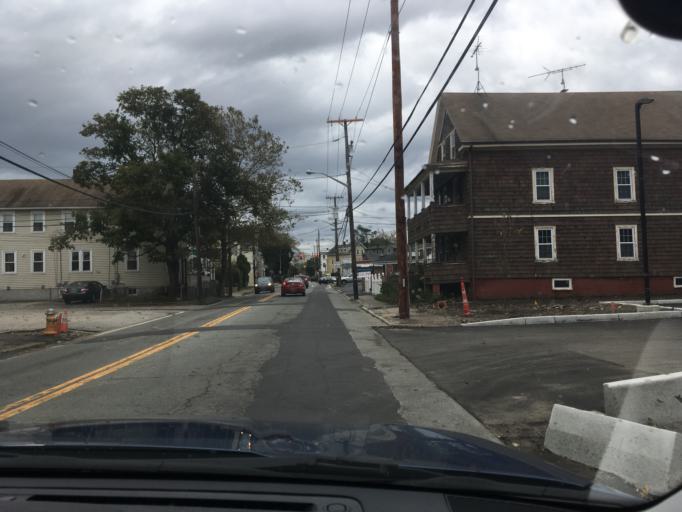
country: US
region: Rhode Island
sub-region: Bristol County
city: Warren
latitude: 41.7364
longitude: -71.2865
